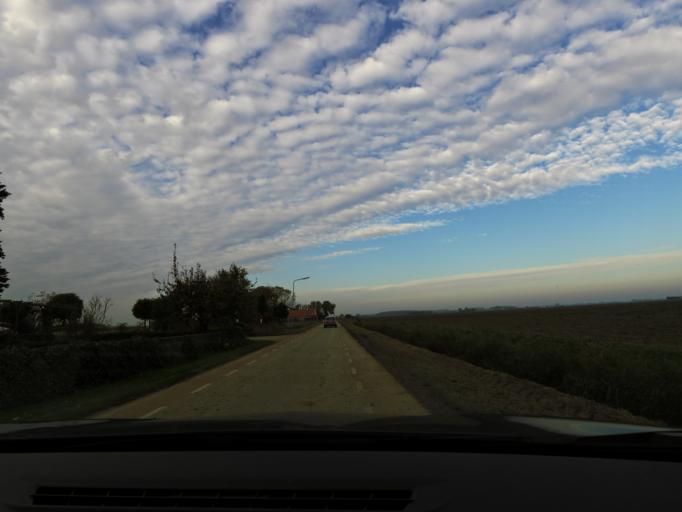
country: NL
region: South Holland
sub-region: Gemeente Goeree-Overflakkee
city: Middelharnis
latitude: 51.7174
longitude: 4.1582
